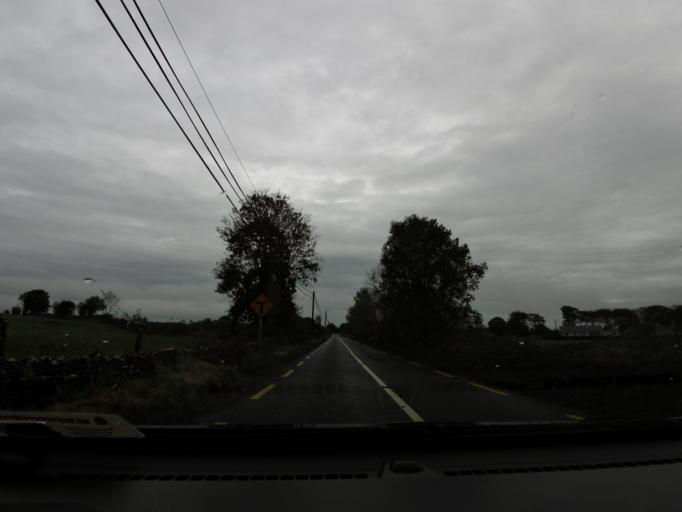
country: IE
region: Connaught
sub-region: County Galway
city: Tuam
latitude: 53.5407
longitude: -8.8133
